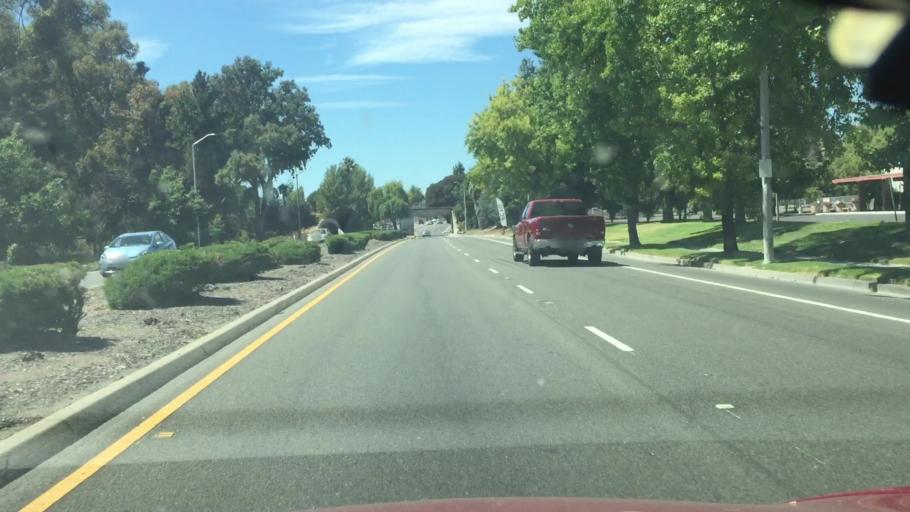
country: US
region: California
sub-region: Alameda County
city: Fremont
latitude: 37.5587
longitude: -121.9539
